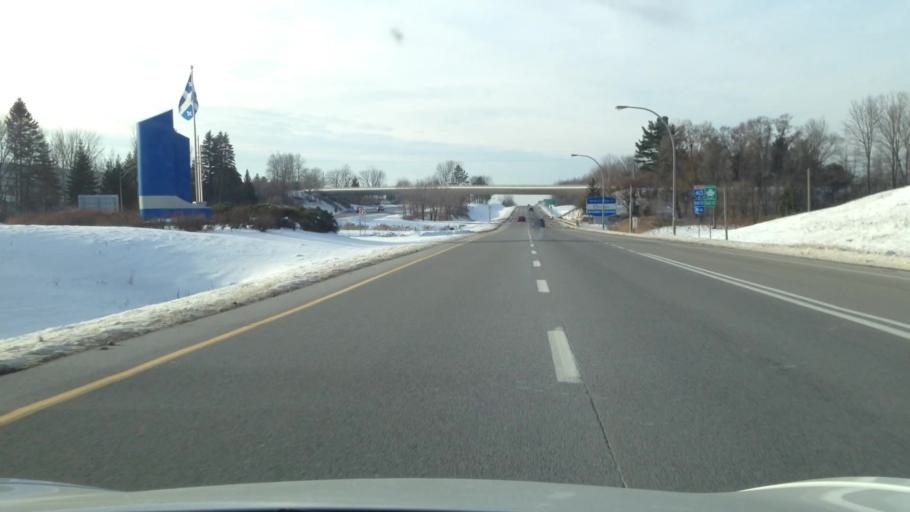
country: CA
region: Quebec
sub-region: Monteregie
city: Rigaud
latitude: 45.5386
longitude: -74.3870
